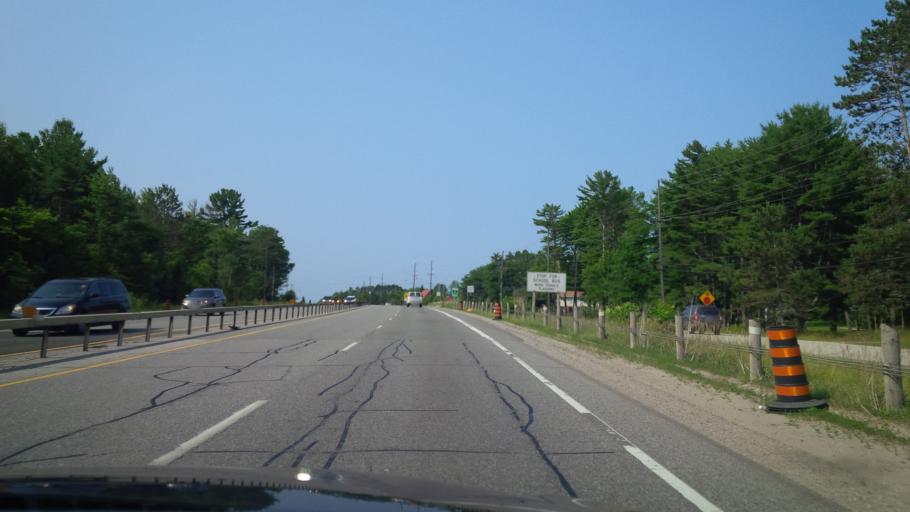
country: CA
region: Ontario
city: Orillia
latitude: 44.7269
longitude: -79.3719
